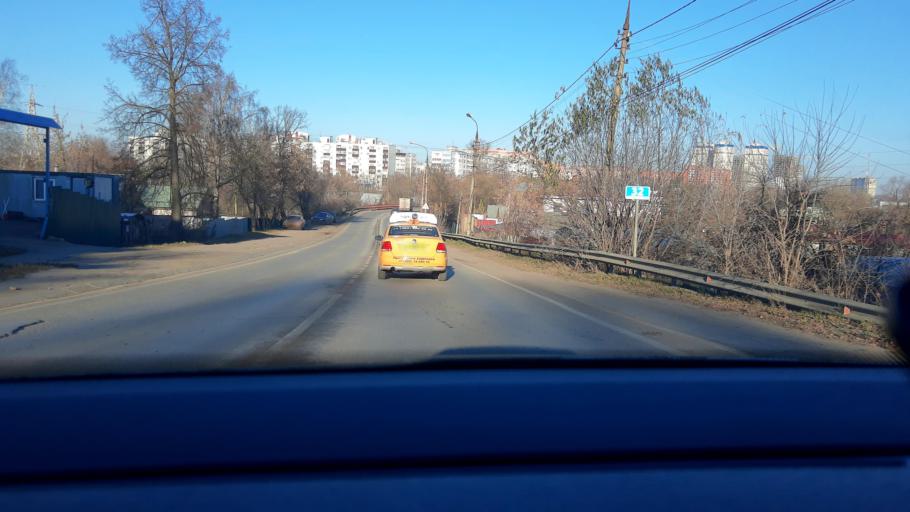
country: RU
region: Moskovskaya
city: Lesnyye Polyany
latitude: 55.9894
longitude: 37.8682
